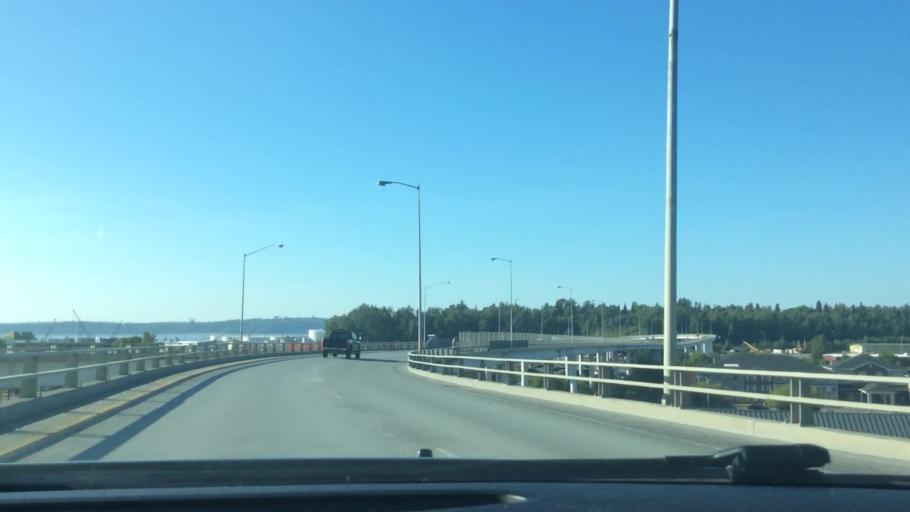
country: US
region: Alaska
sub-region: Anchorage Municipality
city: Anchorage
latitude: 61.2206
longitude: -149.8845
